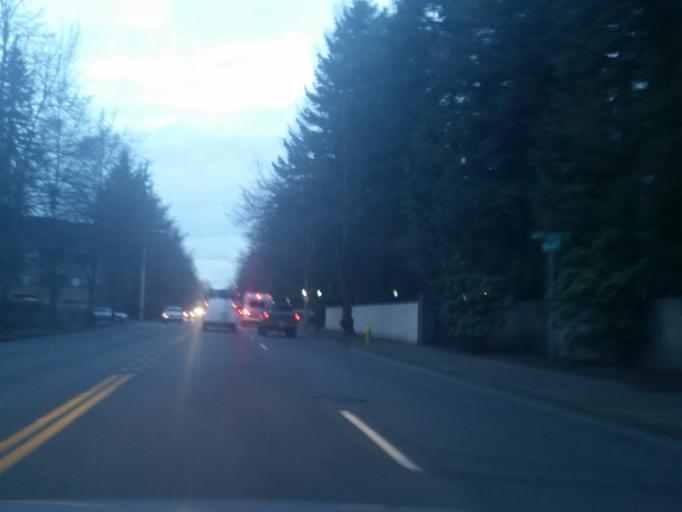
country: US
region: Washington
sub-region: King County
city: Shoreline
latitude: 47.7301
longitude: -122.3127
